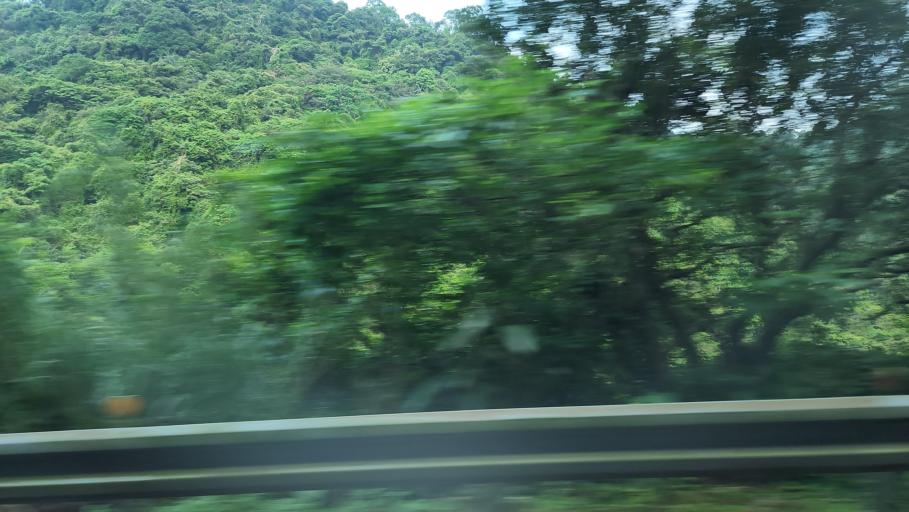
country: TW
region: Taiwan
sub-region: Keelung
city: Keelung
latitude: 25.1620
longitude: 121.6529
